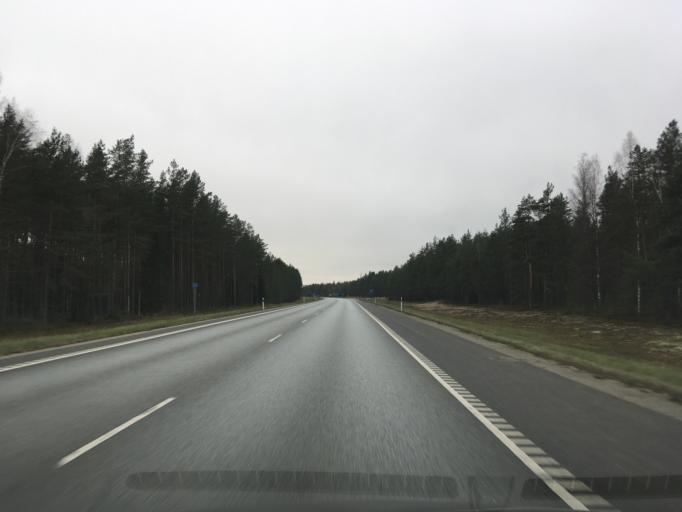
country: EE
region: Harju
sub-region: Loksa linn
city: Loksa
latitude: 59.4585
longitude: 25.8495
